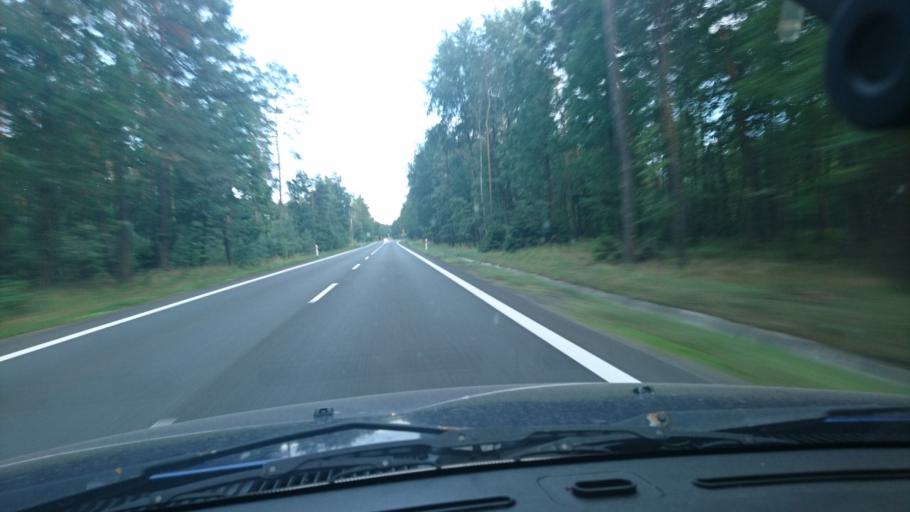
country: PL
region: Silesian Voivodeship
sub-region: Powiat lubliniecki
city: Lubliniec
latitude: 50.6087
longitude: 18.6956
